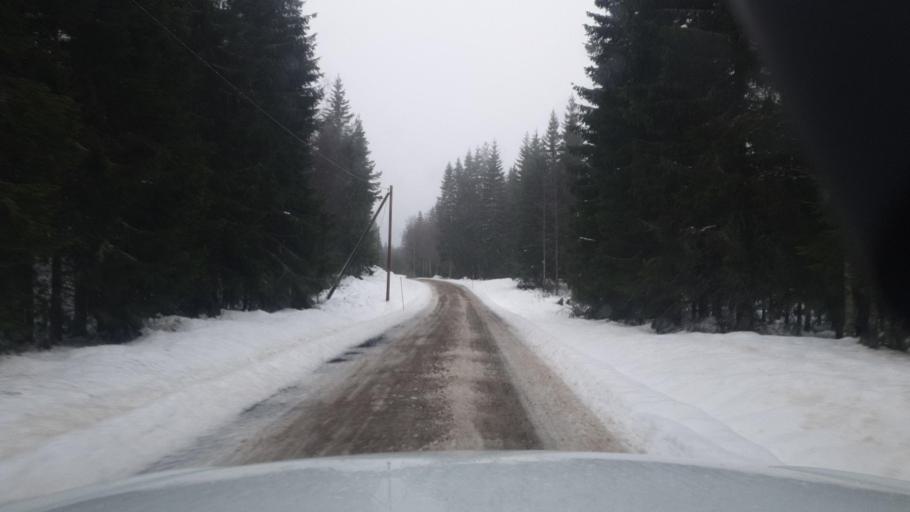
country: SE
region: Vaermland
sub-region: Eda Kommun
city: Charlottenberg
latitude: 60.1599
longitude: 12.6021
